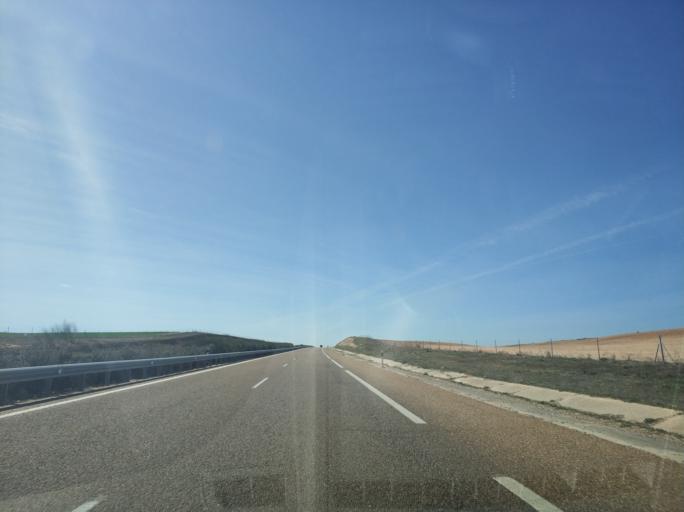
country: ES
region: Castille and Leon
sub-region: Provincia de Valladolid
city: Pollos
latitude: 41.4333
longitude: -5.0999
